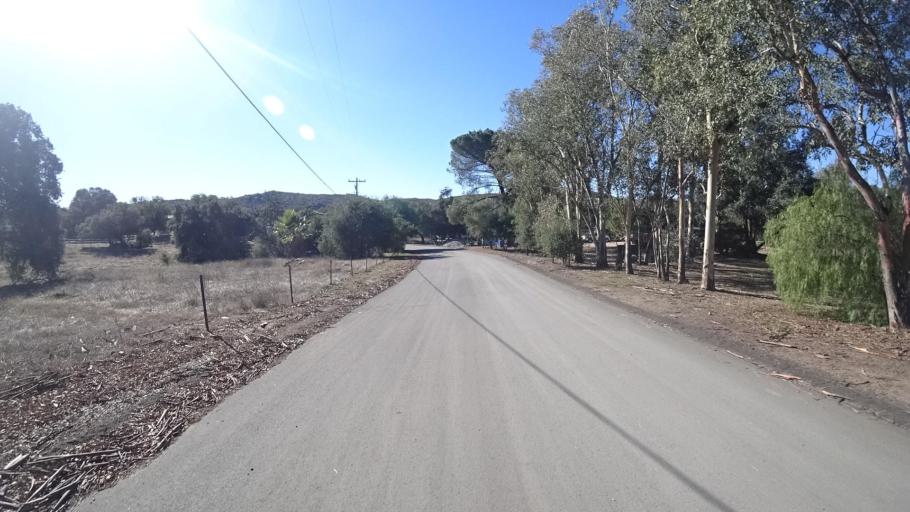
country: MX
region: Baja California
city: Tecate
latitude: 32.6775
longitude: -116.7290
